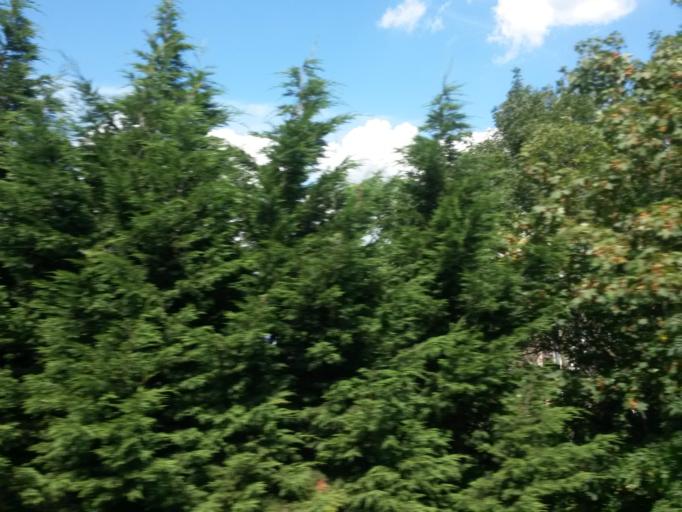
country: GB
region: England
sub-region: Greater London
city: Earlsfield
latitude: 51.4442
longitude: -0.1583
